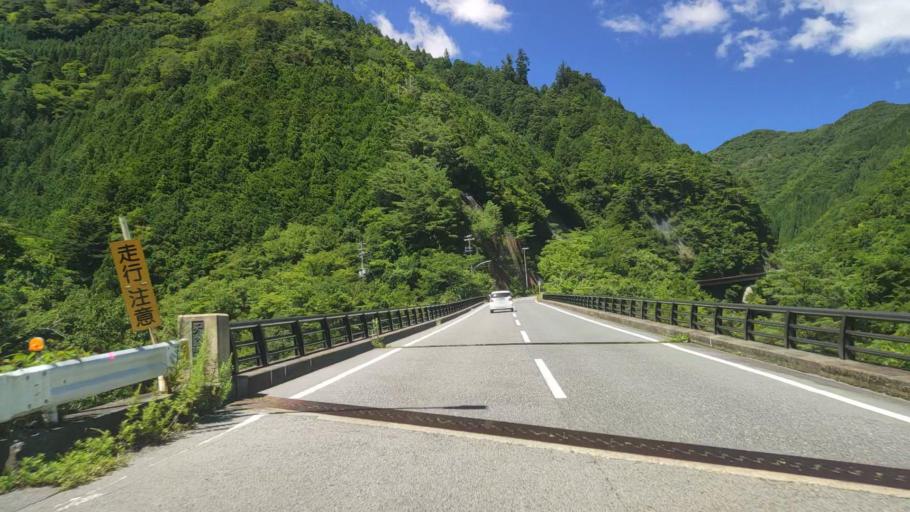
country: JP
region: Mie
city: Owase
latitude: 34.1918
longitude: 135.9939
